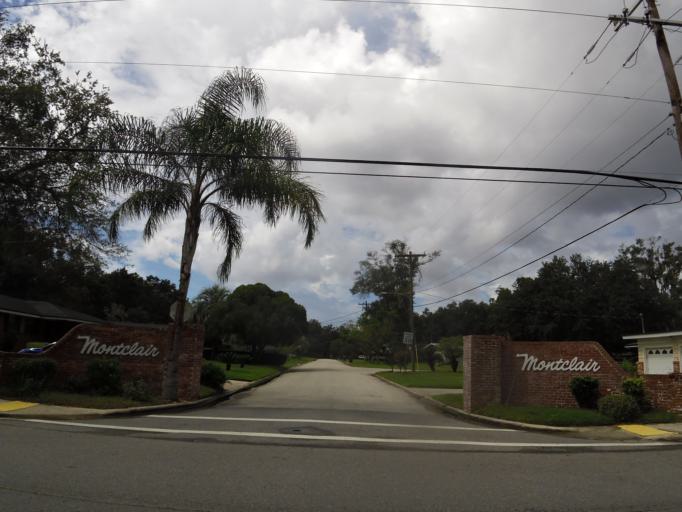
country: US
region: Florida
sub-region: Clay County
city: Orange Park
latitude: 30.2265
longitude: -81.6163
